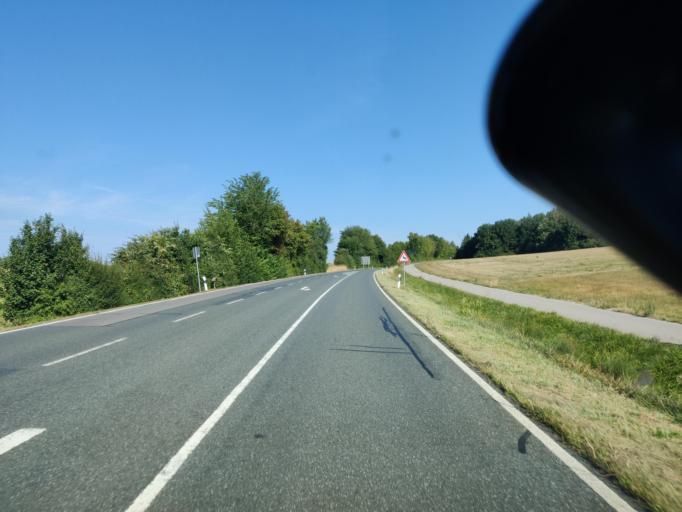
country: DE
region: Bavaria
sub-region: Regierungsbezirk Mittelfranken
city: Hilpoltstein
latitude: 49.1711
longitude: 11.2296
